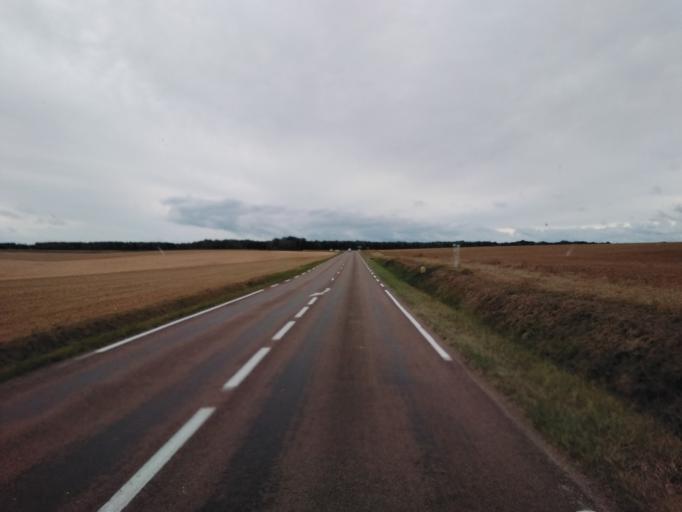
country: FR
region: Champagne-Ardenne
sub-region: Departement de l'Aube
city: Vendeuvre-sur-Barse
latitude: 48.2272
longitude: 4.4551
